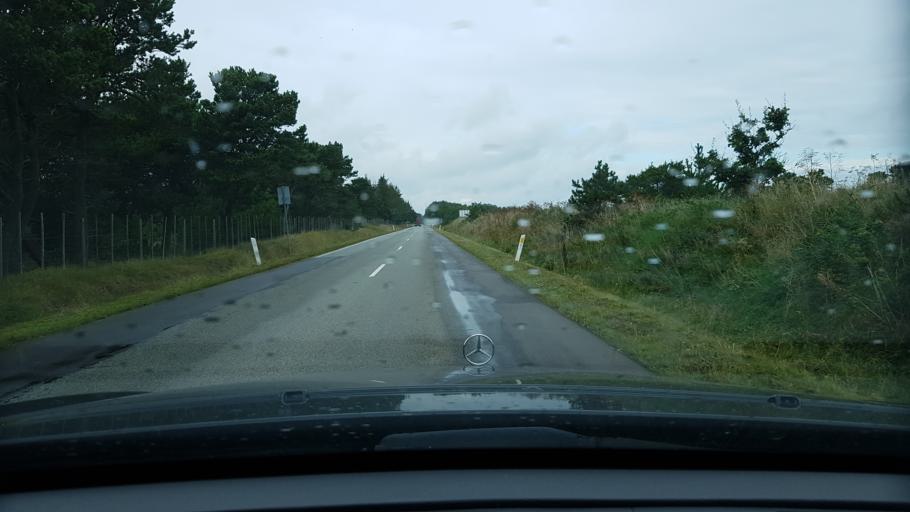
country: DK
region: North Denmark
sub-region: Alborg Kommune
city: Hals
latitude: 56.8272
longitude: 10.2688
